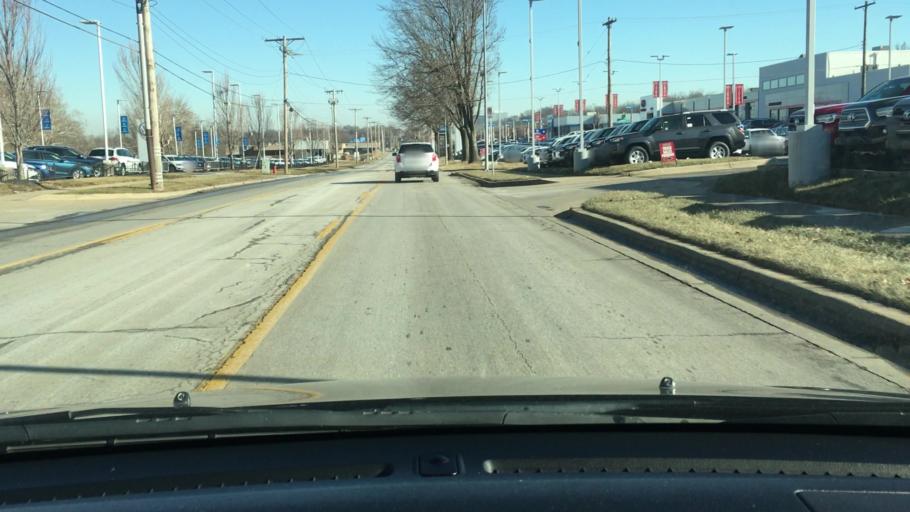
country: US
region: Kansas
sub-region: Johnson County
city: Leawood
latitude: 38.9417
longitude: -94.6020
